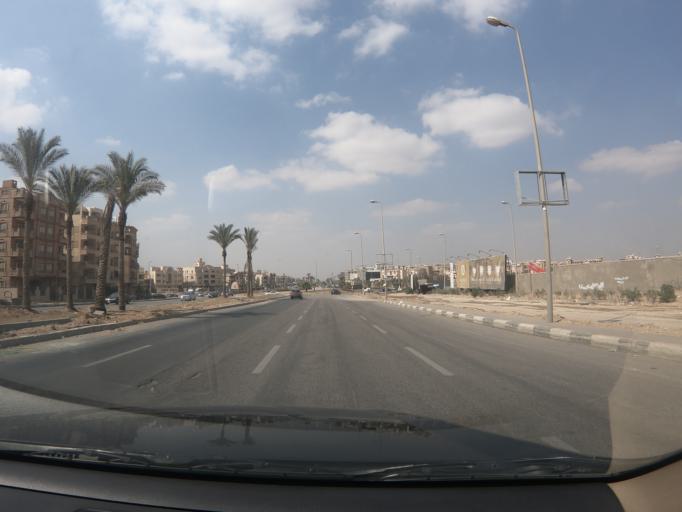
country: EG
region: Muhafazat al Qalyubiyah
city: Al Khankah
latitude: 30.0345
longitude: 31.4748
